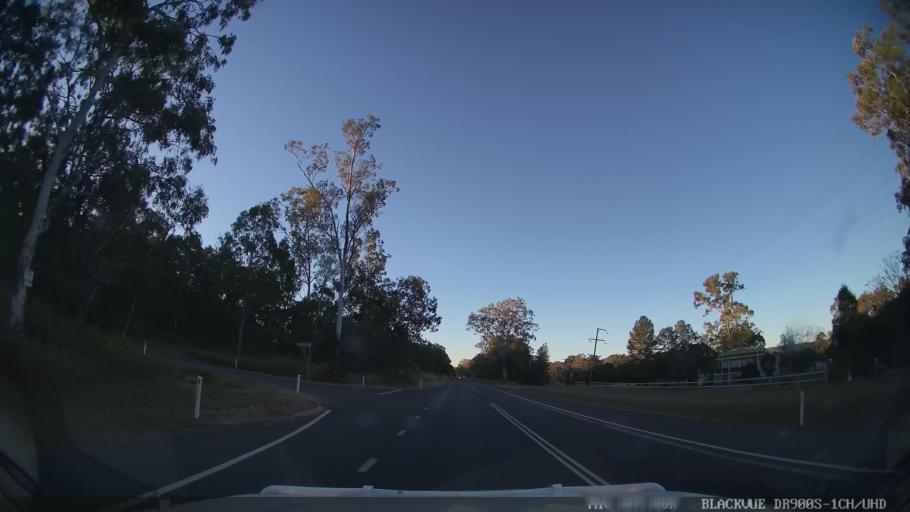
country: AU
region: Queensland
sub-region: Gladstone
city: Toolooa
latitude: -23.9605
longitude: 151.2185
